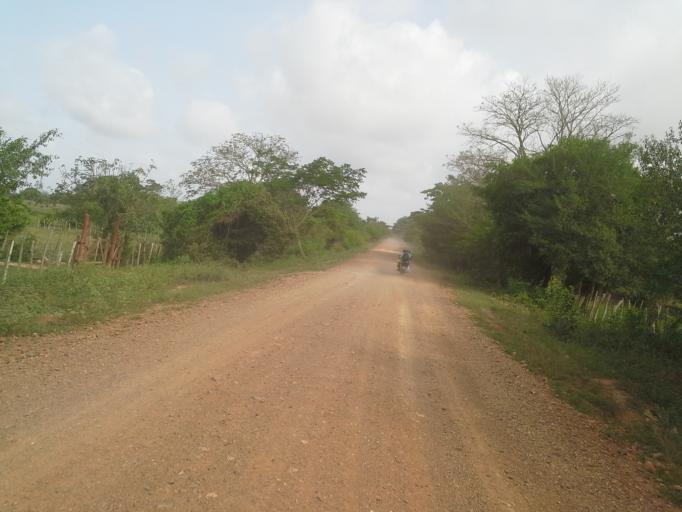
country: CO
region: Cordoba
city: Chima
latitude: 9.1438
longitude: -75.6159
